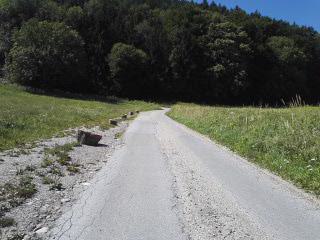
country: AT
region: Styria
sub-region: Politischer Bezirk Graz-Umgebung
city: Frohnleiten
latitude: 47.2313
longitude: 15.3185
